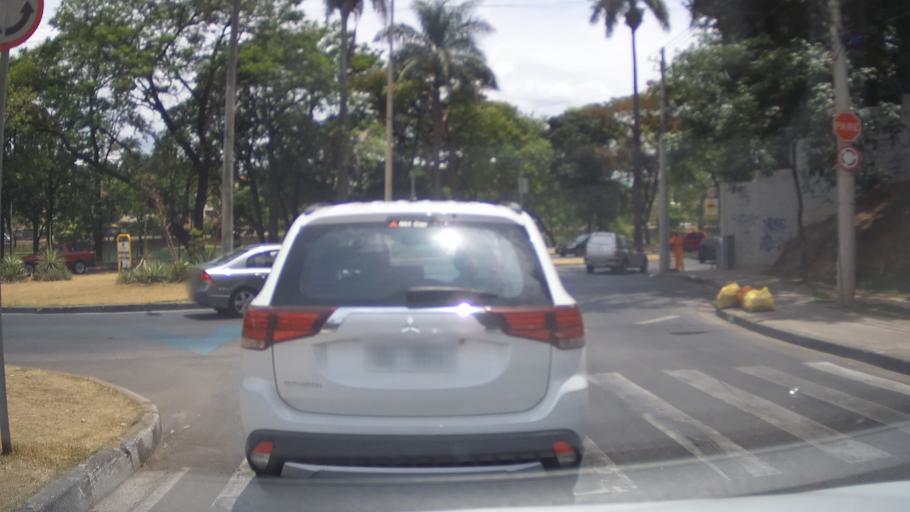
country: BR
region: Minas Gerais
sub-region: Belo Horizonte
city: Belo Horizonte
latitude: -19.8608
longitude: -43.9748
